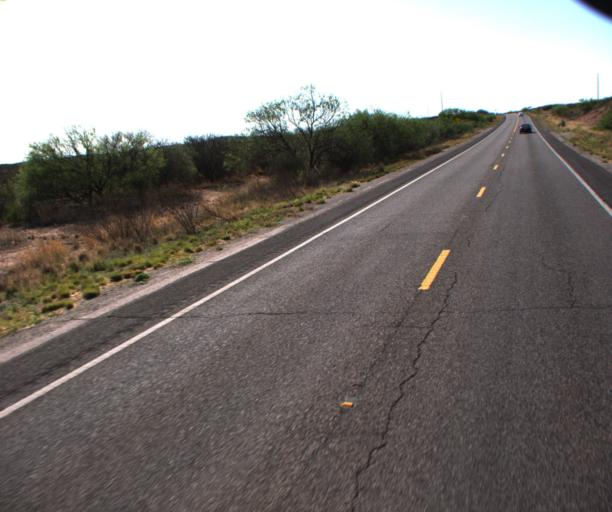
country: US
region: Arizona
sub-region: Cochise County
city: Tombstone
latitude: 31.7887
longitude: -110.1487
